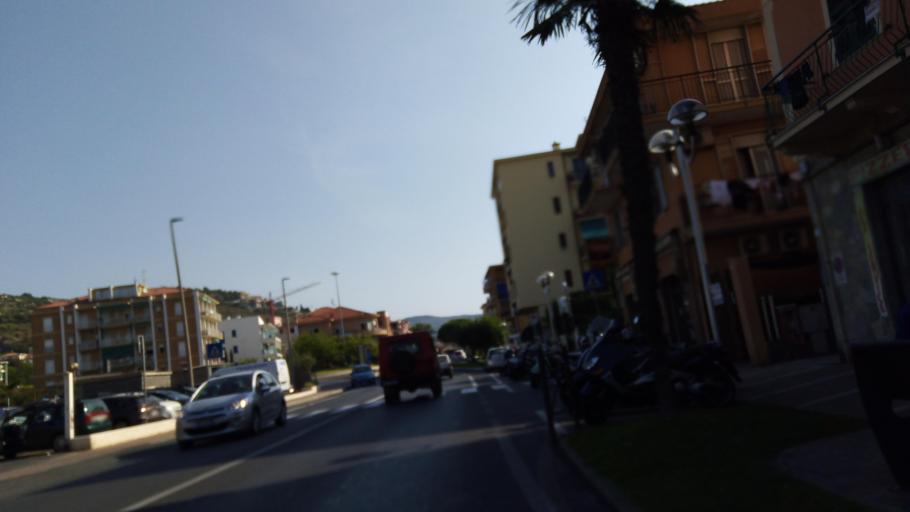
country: IT
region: Liguria
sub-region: Provincia di Savona
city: Pietra Ligure
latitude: 44.1438
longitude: 8.2744
